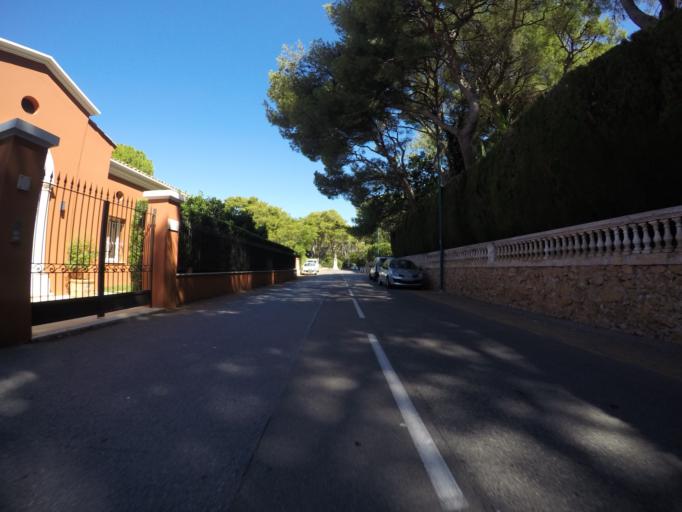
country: FR
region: Provence-Alpes-Cote d'Azur
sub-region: Departement des Alpes-Maritimes
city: Saint-Jean-Cap-Ferrat
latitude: 43.6875
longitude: 7.3242
